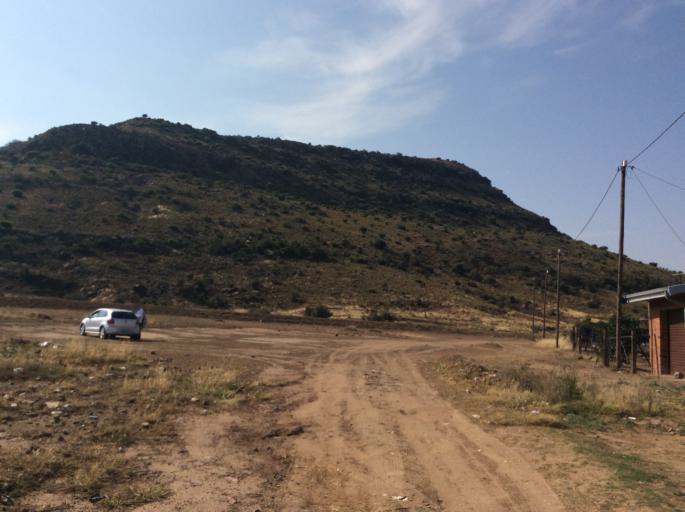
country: LS
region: Mafeteng
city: Mafeteng
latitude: -29.7181
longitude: 27.0354
